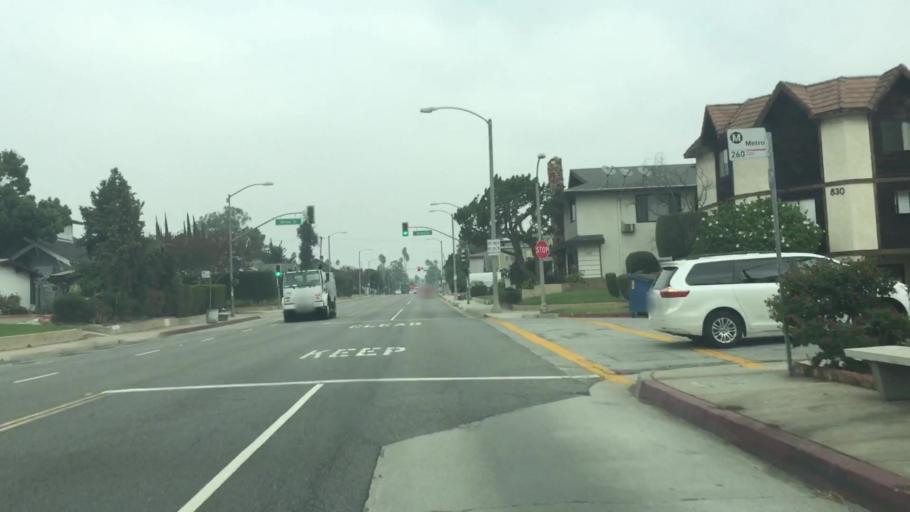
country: US
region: California
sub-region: Los Angeles County
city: Alhambra
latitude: 34.1019
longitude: -118.1347
